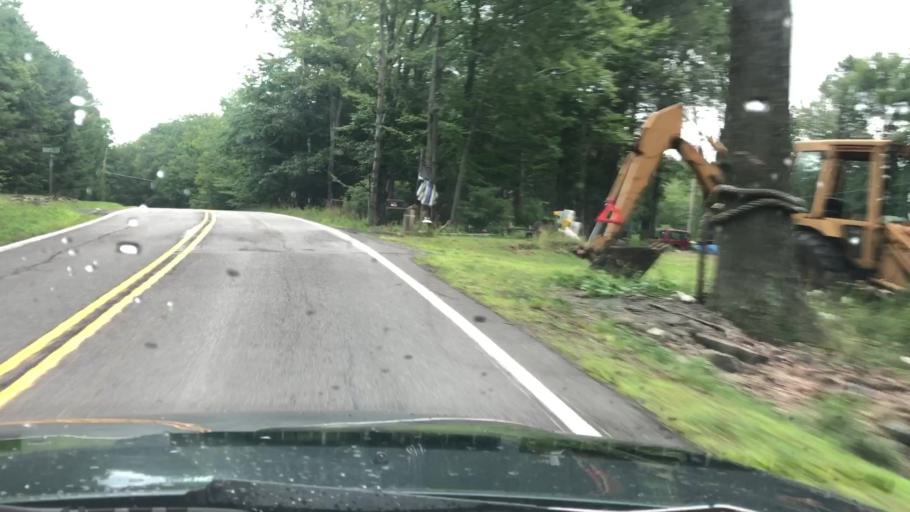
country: US
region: Pennsylvania
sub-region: Monroe County
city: Mountainhome
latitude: 41.2872
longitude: -75.2265
